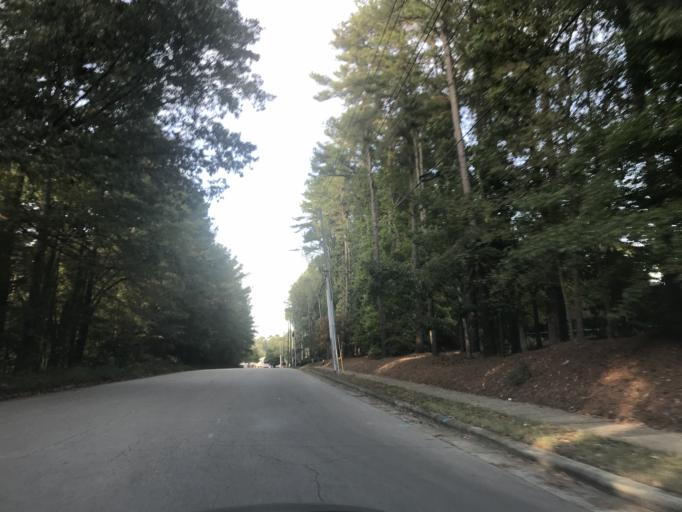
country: US
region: North Carolina
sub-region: Wake County
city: Raleigh
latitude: 35.8309
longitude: -78.6122
